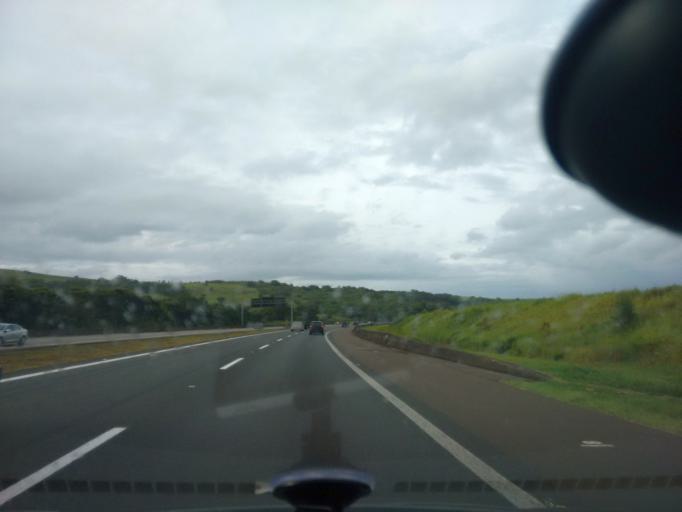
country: BR
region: Sao Paulo
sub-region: Limeira
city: Limeira
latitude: -22.5453
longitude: -47.4617
